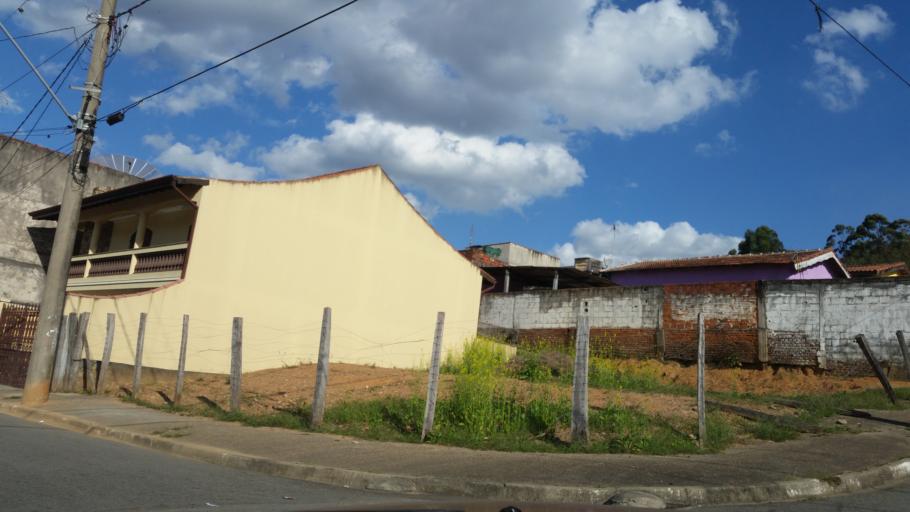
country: BR
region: Sao Paulo
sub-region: Mairinque
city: Mairinque
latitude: -23.5173
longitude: -47.2608
